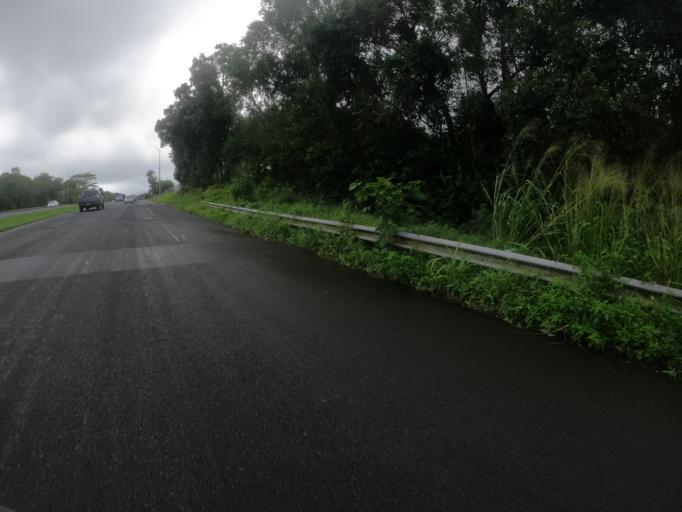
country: US
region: Hawaii
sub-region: Honolulu County
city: Maunawili
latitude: 21.3840
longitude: -157.7899
